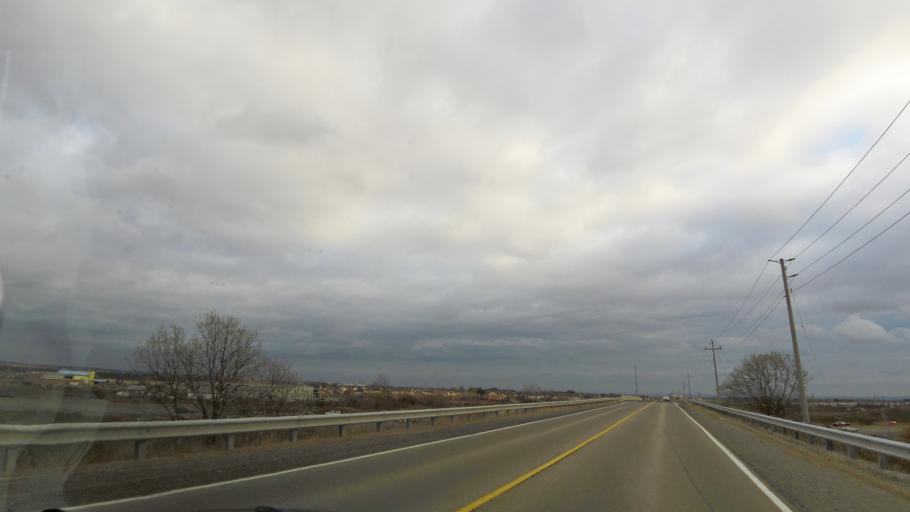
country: CA
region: Ontario
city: Burlington
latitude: 43.3999
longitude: -79.8344
